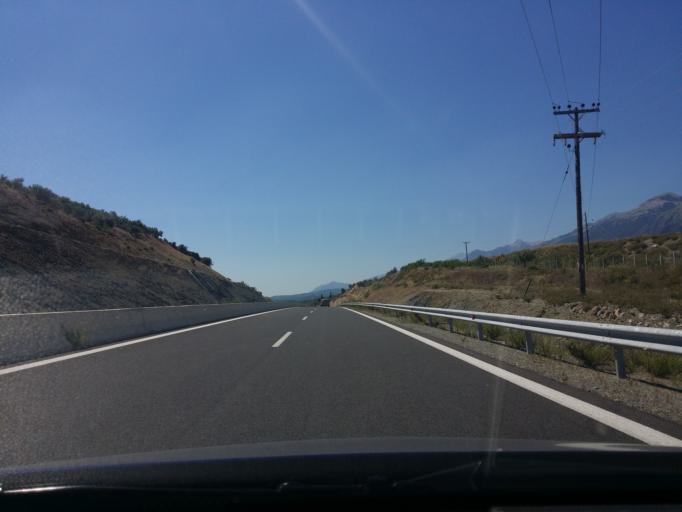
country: GR
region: Peloponnese
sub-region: Nomos Lakonias
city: Magoula
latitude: 37.2205
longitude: 22.3202
